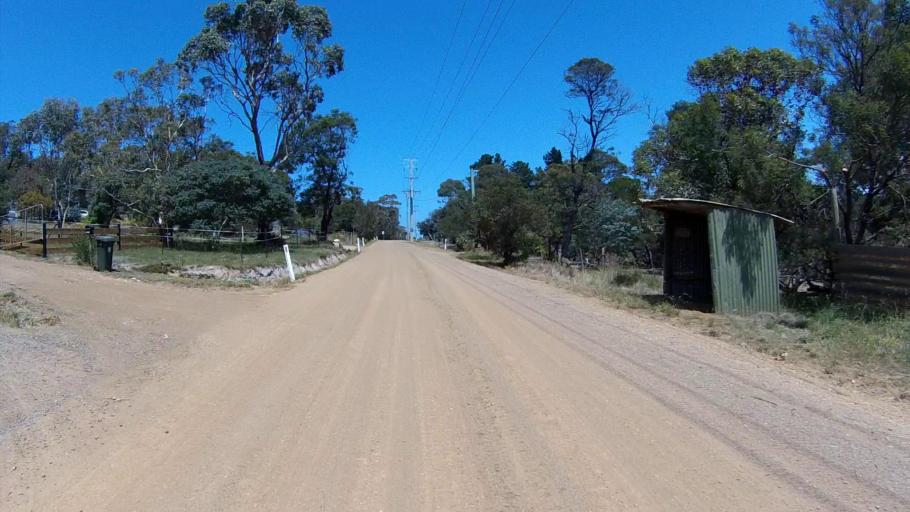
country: AU
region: Tasmania
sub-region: Clarence
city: Lauderdale
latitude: -42.9376
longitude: 147.4606
